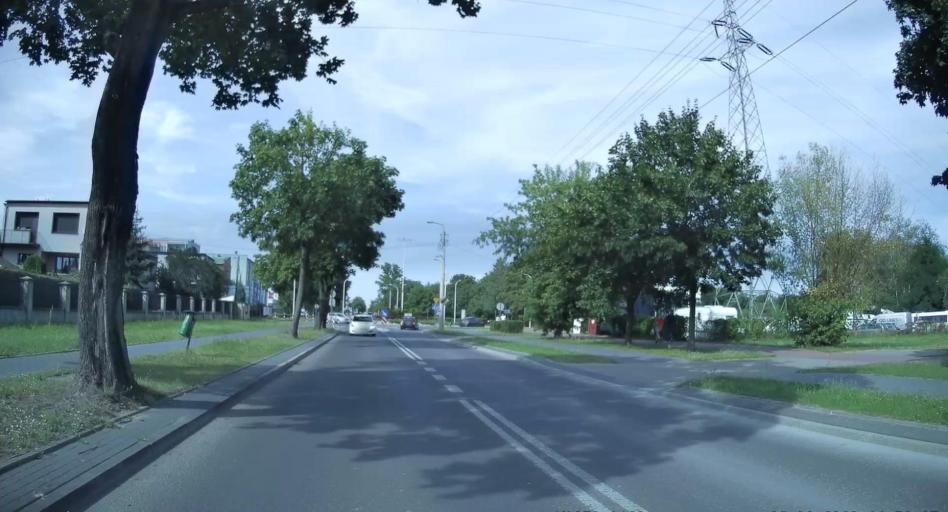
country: PL
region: Lodz Voivodeship
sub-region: Powiat tomaszowski
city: Tomaszow Mazowiecki
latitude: 51.5203
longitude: 20.0028
